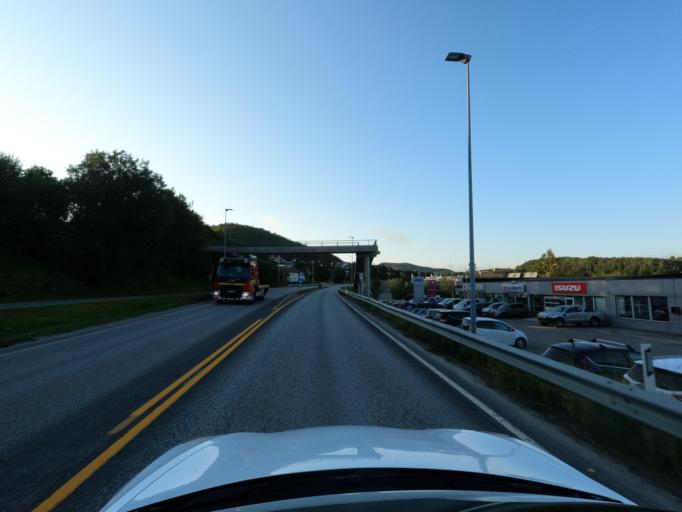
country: NO
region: Troms
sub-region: Harstad
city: Harstad
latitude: 68.7706
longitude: 16.5578
